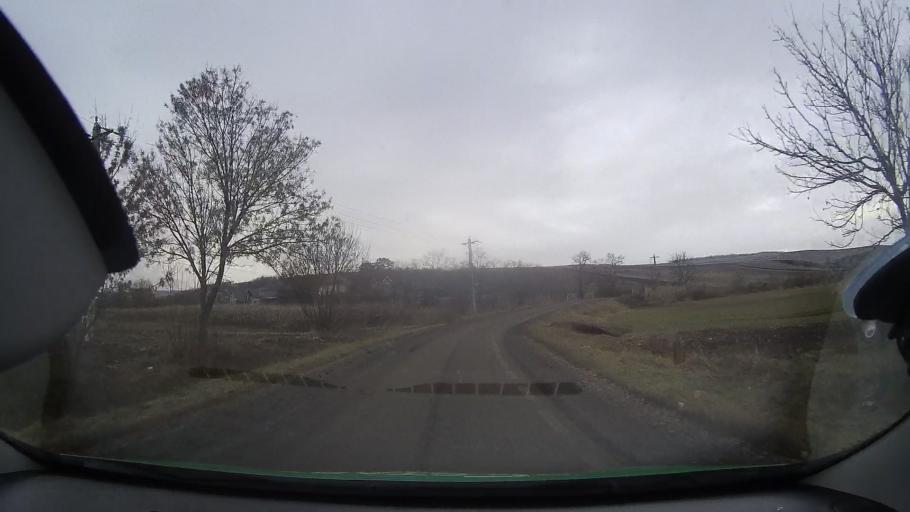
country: RO
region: Mures
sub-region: Comuna Bichis
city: Bichis
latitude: 46.3830
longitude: 24.0807
